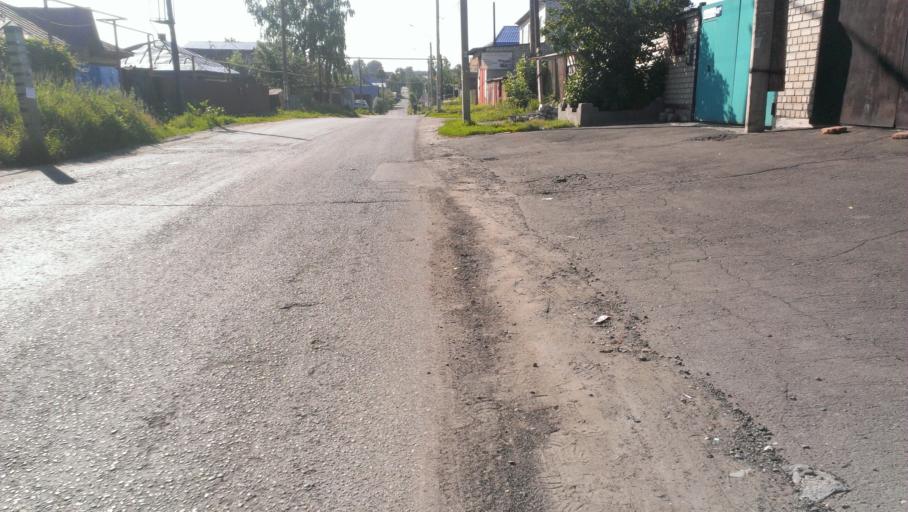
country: RU
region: Altai Krai
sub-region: Gorod Barnaulskiy
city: Barnaul
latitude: 53.3564
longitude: 83.7474
